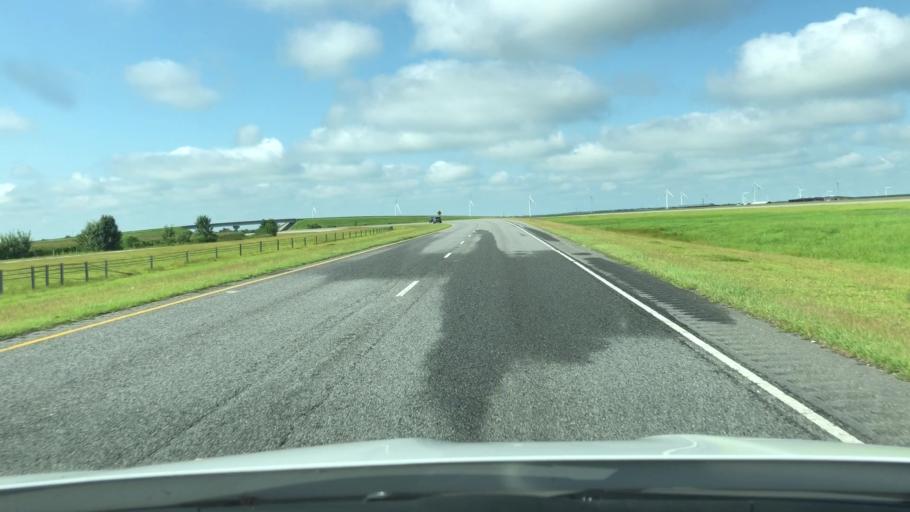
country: US
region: North Carolina
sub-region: Pasquotank County
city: Elizabeth City
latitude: 36.3675
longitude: -76.3141
